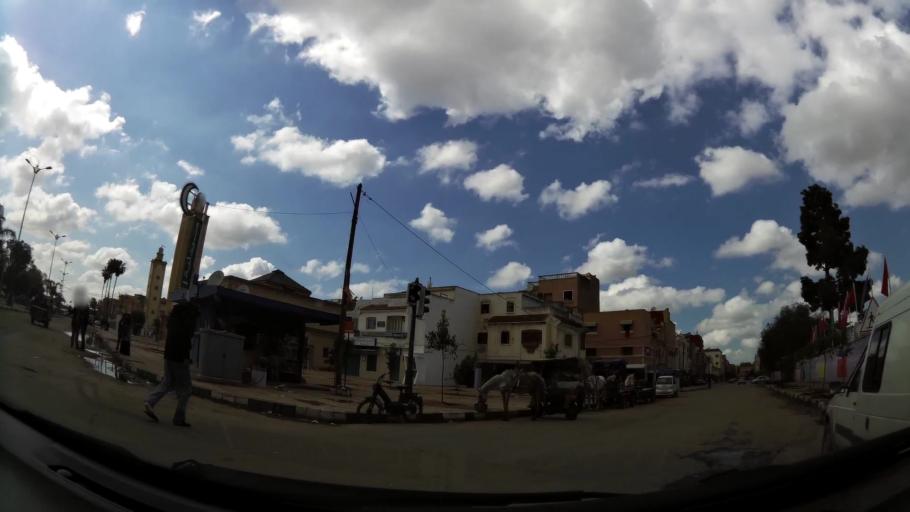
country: MA
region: Grand Casablanca
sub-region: Mediouna
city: Mediouna
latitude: 33.3732
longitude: -7.5338
